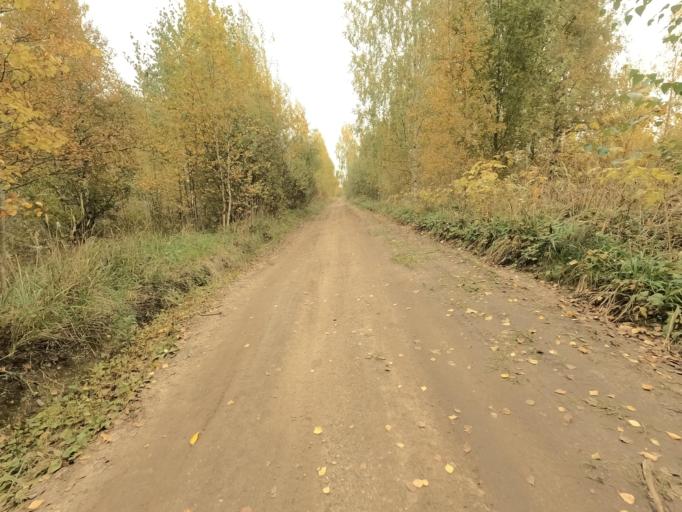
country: RU
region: Novgorod
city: Pankovka
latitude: 58.8665
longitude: 30.9230
